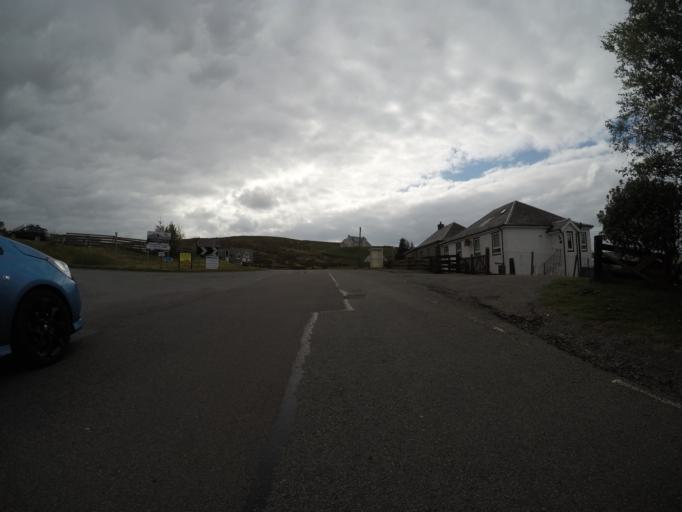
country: GB
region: Scotland
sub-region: Highland
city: Isle of Skye
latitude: 57.2951
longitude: -6.3338
